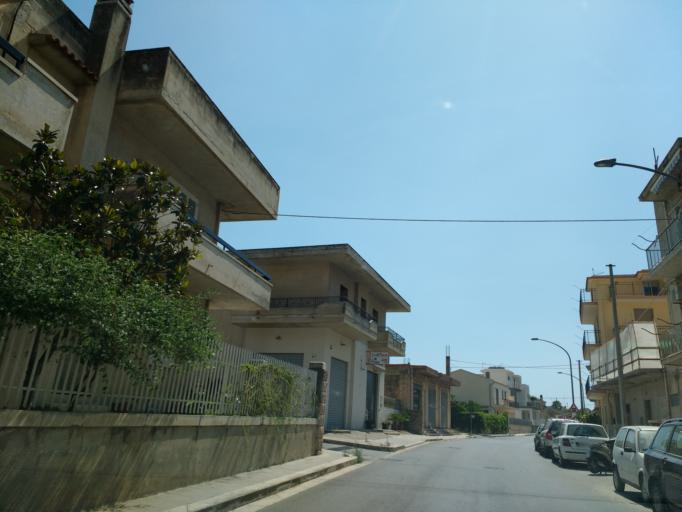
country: IT
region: Sicily
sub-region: Ragusa
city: Scicli
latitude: 36.7840
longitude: 14.6940
